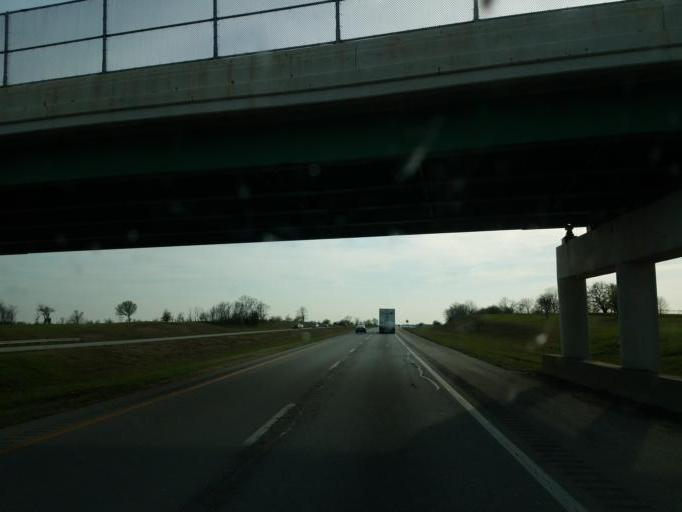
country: US
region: Ohio
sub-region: Greene County
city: Jamestown
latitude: 39.5578
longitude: -83.7191
